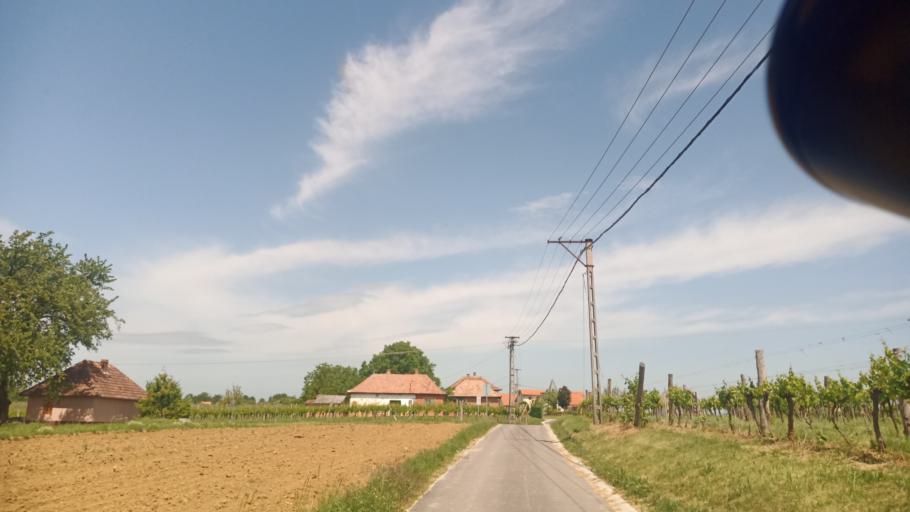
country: HU
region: Zala
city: Zalakomar
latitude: 46.6146
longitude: 17.1023
